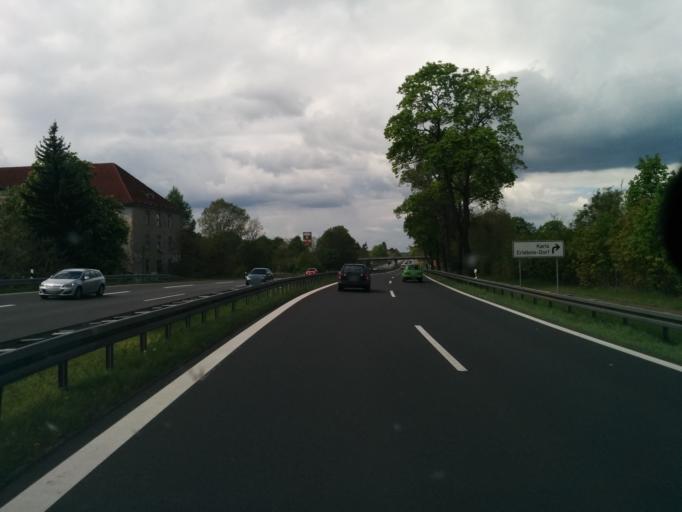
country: DE
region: Brandenburg
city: Brieselang
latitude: 52.5331
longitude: 13.0040
